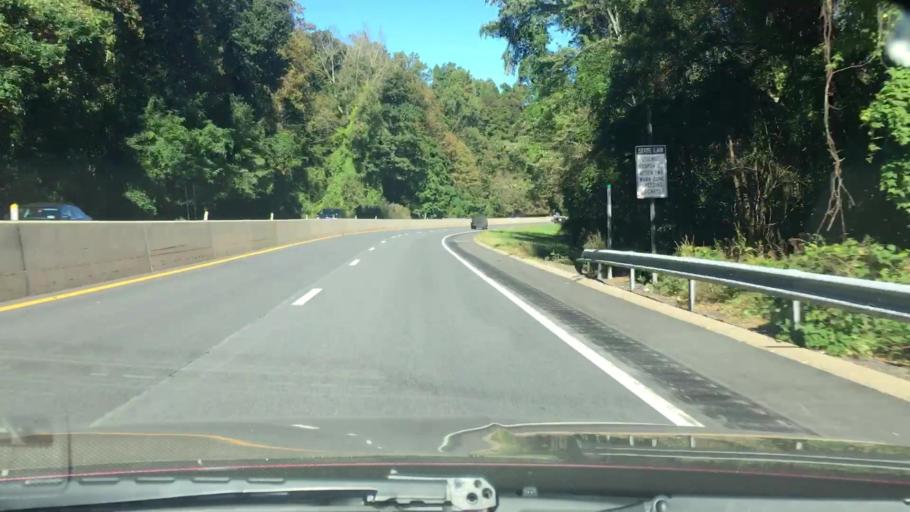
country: US
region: New York
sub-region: Westchester County
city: Chappaqua
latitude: 41.1525
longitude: -73.7811
